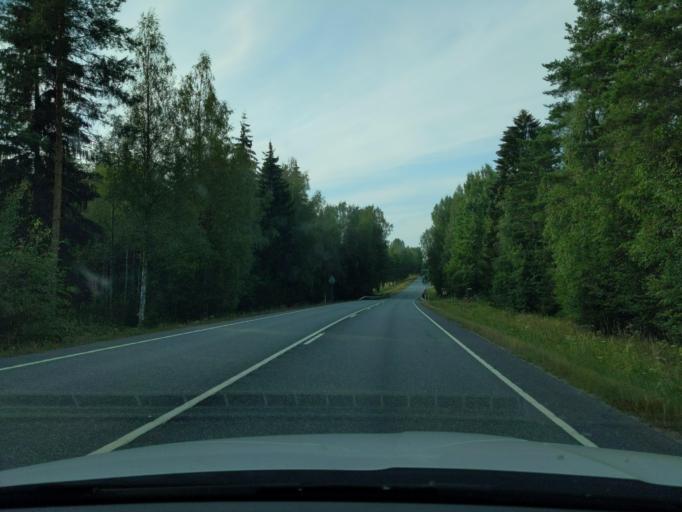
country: FI
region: Paijanne Tavastia
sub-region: Lahti
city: Padasjoki
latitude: 61.2971
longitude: 25.3030
